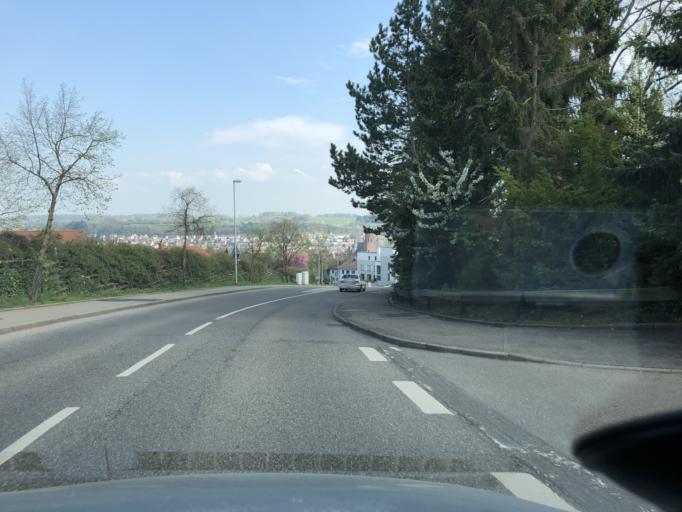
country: DE
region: Baden-Wuerttemberg
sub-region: Regierungsbezirk Stuttgart
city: Weil der Stadt
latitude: 48.7526
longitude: 8.8624
